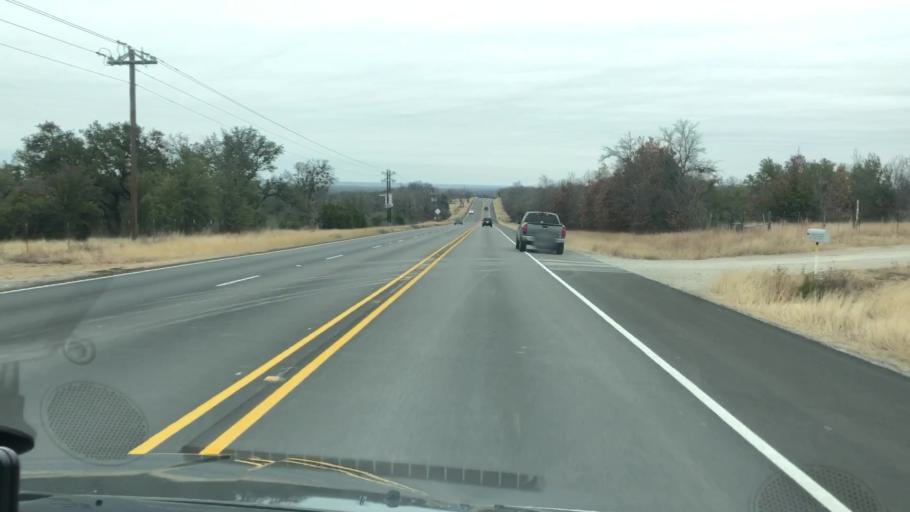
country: US
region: Texas
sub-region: Erath County
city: Stephenville
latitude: 32.4953
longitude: -98.1339
